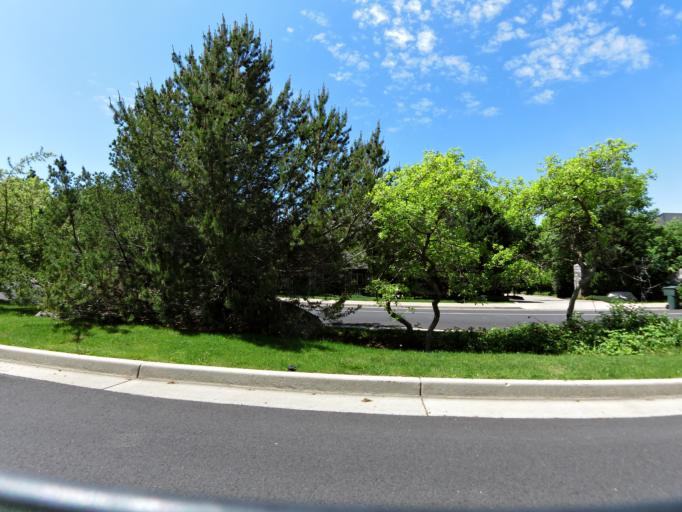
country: US
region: Utah
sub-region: Weber County
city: Uintah
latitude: 41.1687
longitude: -111.9273
